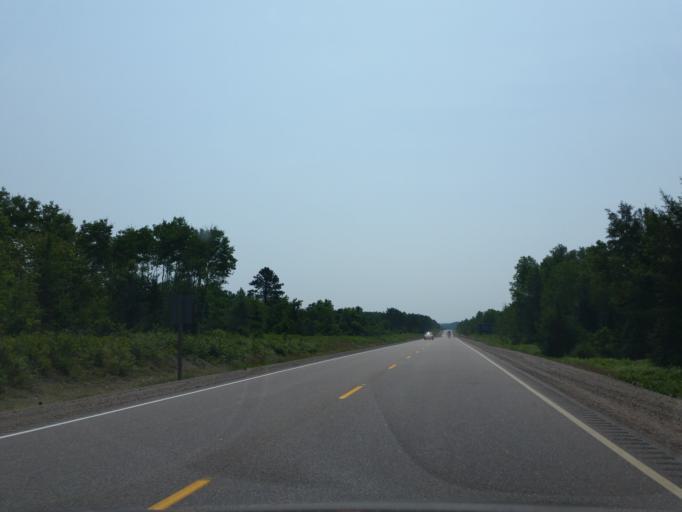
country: CA
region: Ontario
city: Mattawa
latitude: 46.2756
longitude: -78.3724
